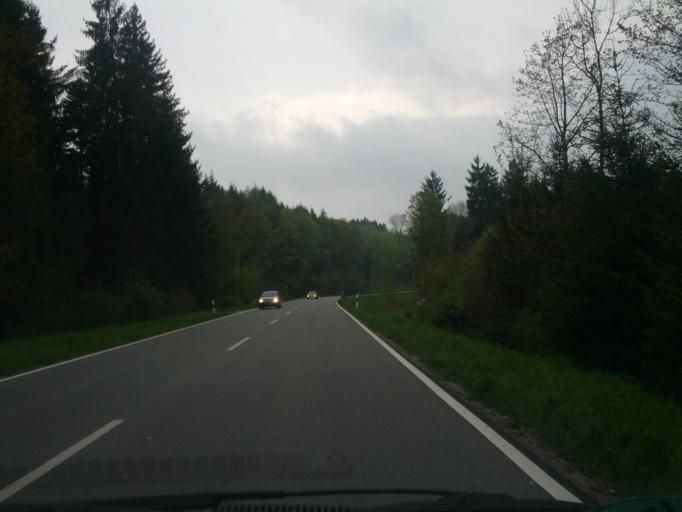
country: DE
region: Baden-Wuerttemberg
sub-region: Freiburg Region
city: Hasel
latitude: 47.6467
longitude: 7.8713
